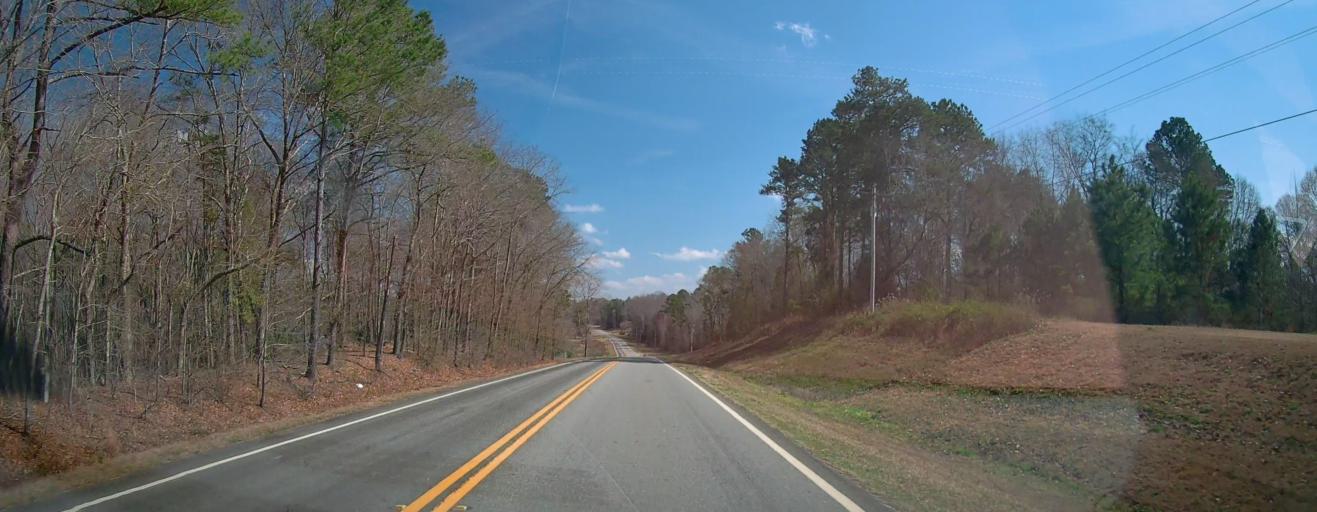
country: US
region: Georgia
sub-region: Wilkinson County
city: Gordon
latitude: 32.9045
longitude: -83.3750
